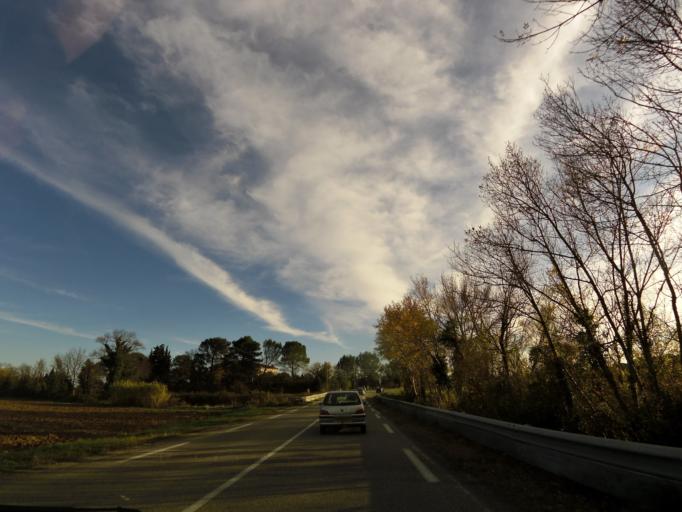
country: FR
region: Languedoc-Roussillon
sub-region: Departement du Gard
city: Ledignan
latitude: 43.9705
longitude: 4.1002
